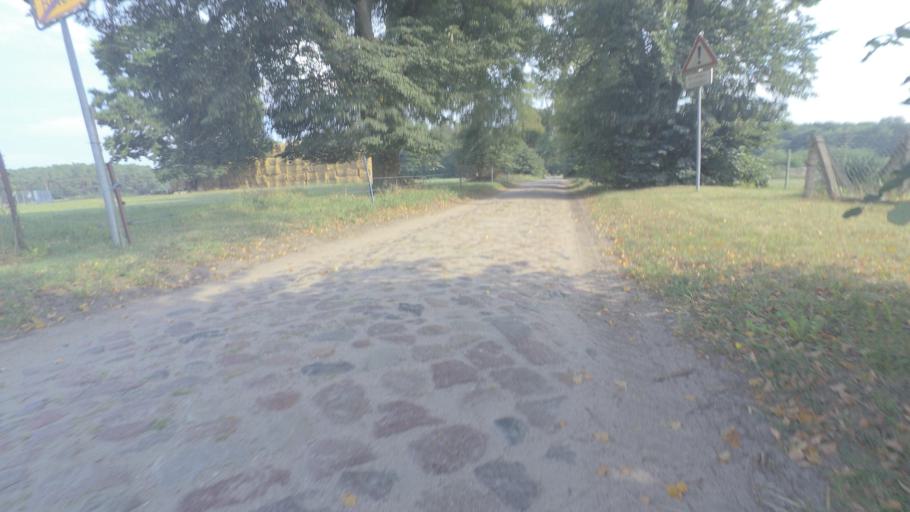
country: DE
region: Brandenburg
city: Wittstock
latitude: 53.2588
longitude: 12.4648
